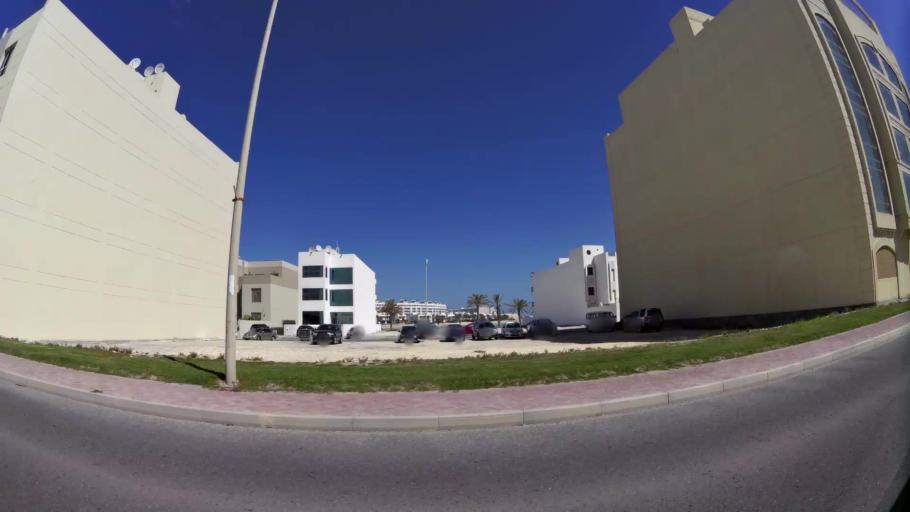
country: BH
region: Muharraq
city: Al Hadd
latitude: 26.2968
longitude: 50.6581
